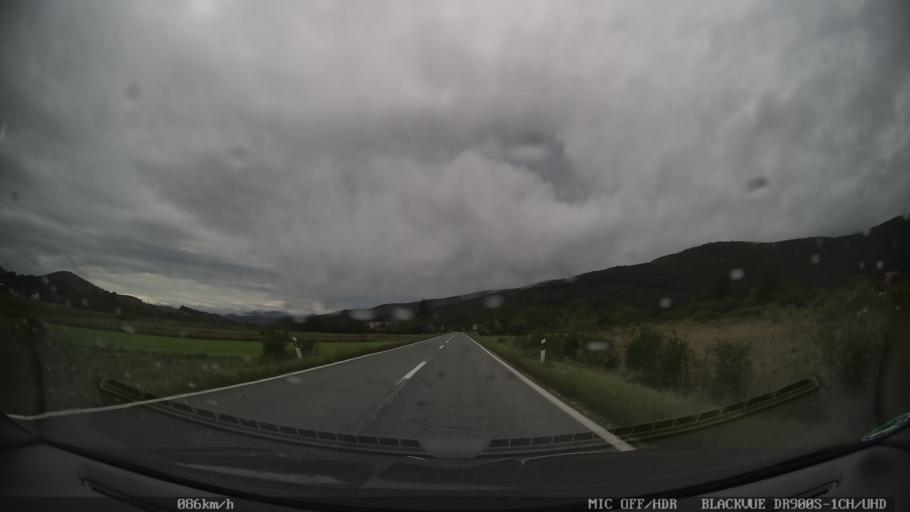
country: HR
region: Licko-Senjska
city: Brinje
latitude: 44.9445
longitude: 15.1259
